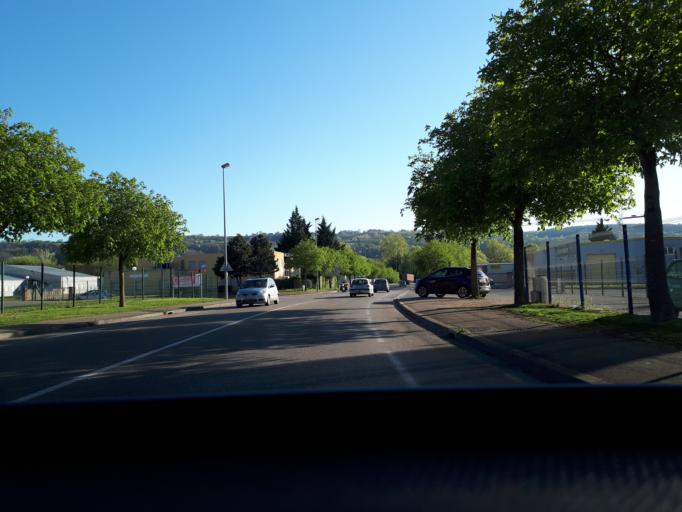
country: FR
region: Rhone-Alpes
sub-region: Departement de l'Isere
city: Bourgoin-Jallieu
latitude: 45.5941
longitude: 5.2649
